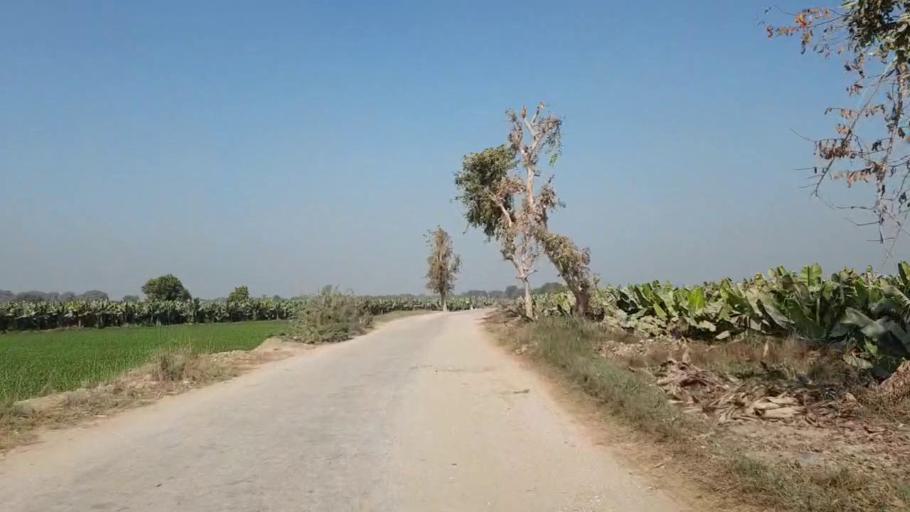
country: PK
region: Sindh
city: Matiari
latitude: 25.6010
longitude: 68.5999
